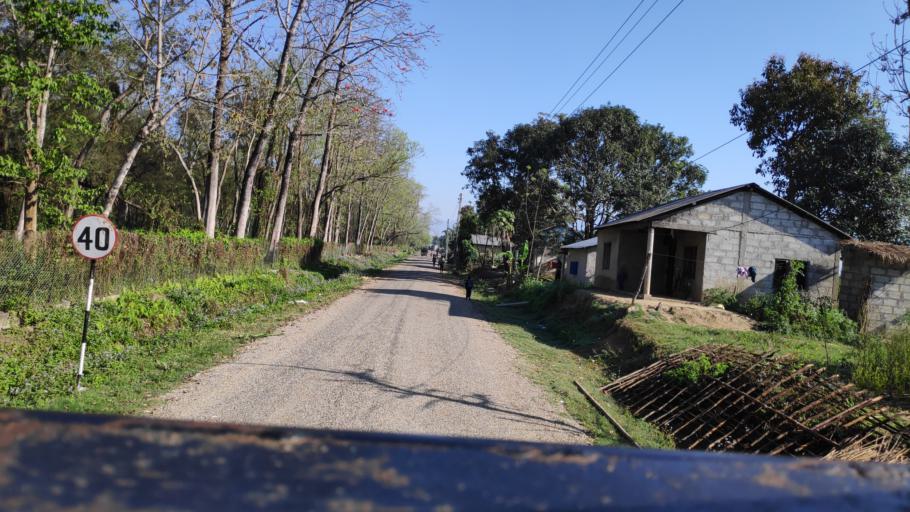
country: NP
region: Central Region
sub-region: Narayani Zone
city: Bharatpur
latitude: 27.5714
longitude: 84.5175
